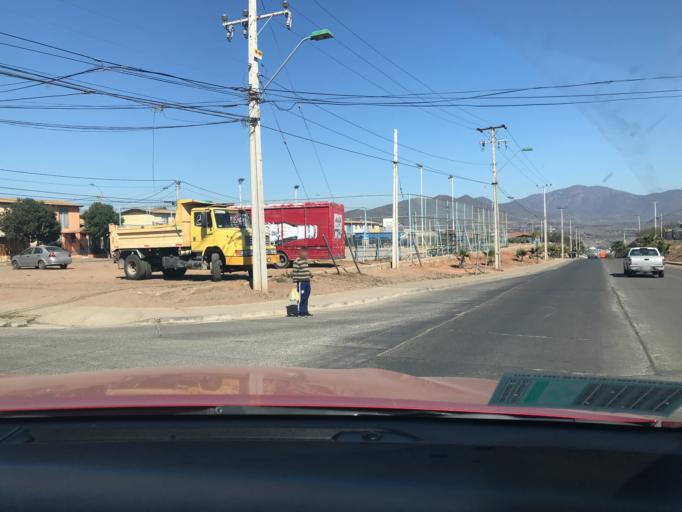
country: CL
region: Coquimbo
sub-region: Provincia de Limari
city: Ovalle
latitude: -30.5850
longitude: -71.1900
